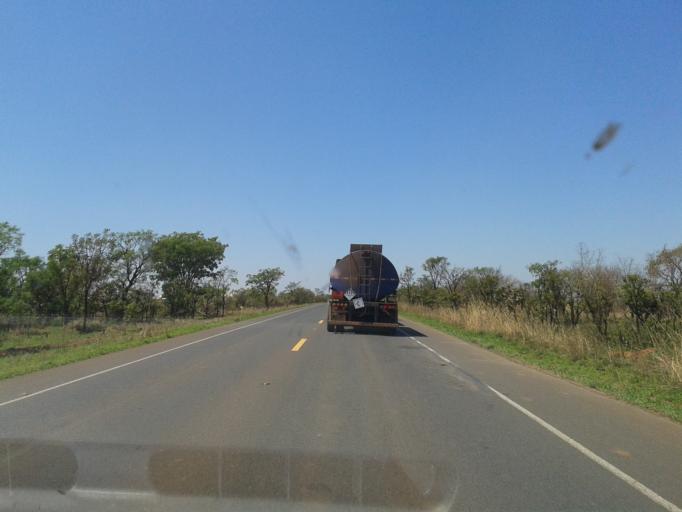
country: BR
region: Minas Gerais
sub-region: Araxa
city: Araxa
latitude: -19.3045
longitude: -47.3945
